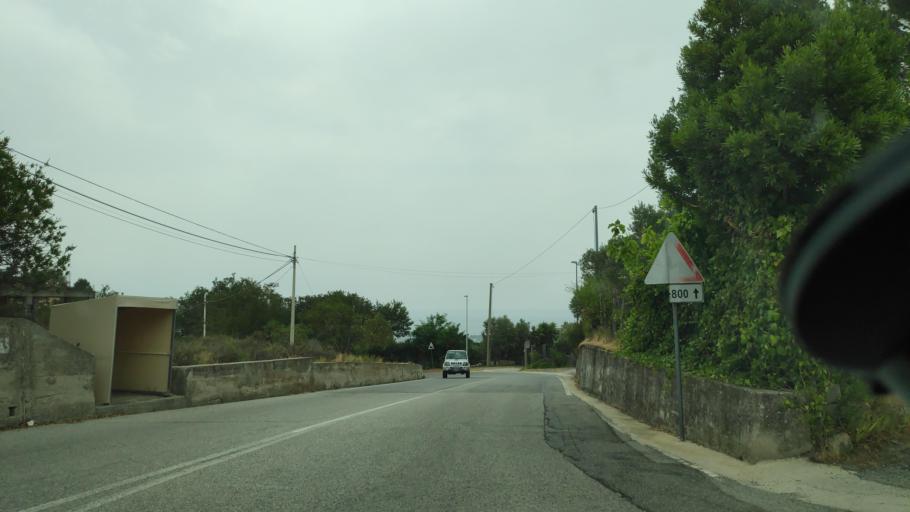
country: IT
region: Calabria
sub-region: Provincia di Catanzaro
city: Davoli
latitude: 38.6617
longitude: 16.5028
